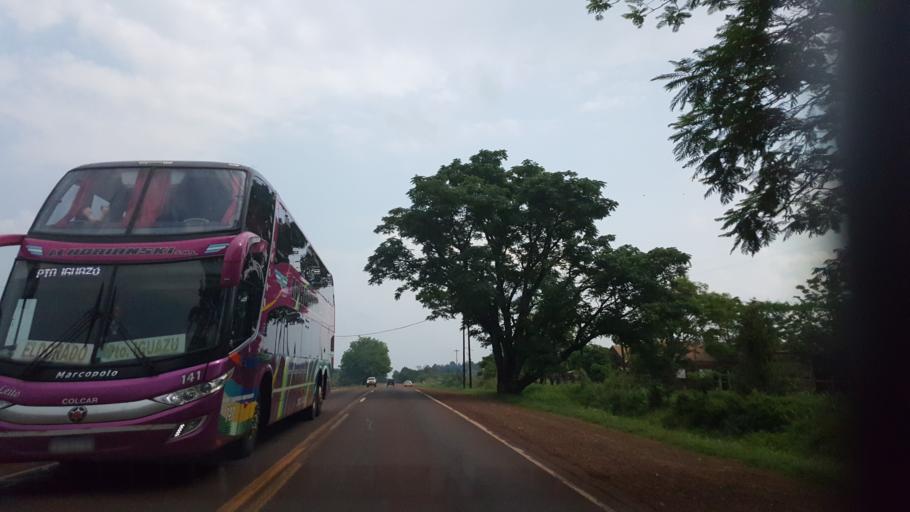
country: AR
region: Misiones
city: Jardin America
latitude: -27.0603
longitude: -55.2595
